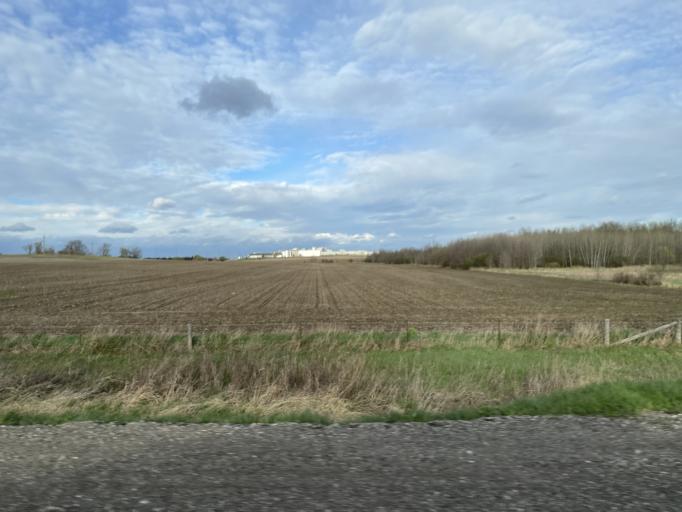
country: CA
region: Ontario
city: Waterloo
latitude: 43.4712
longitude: -80.4017
